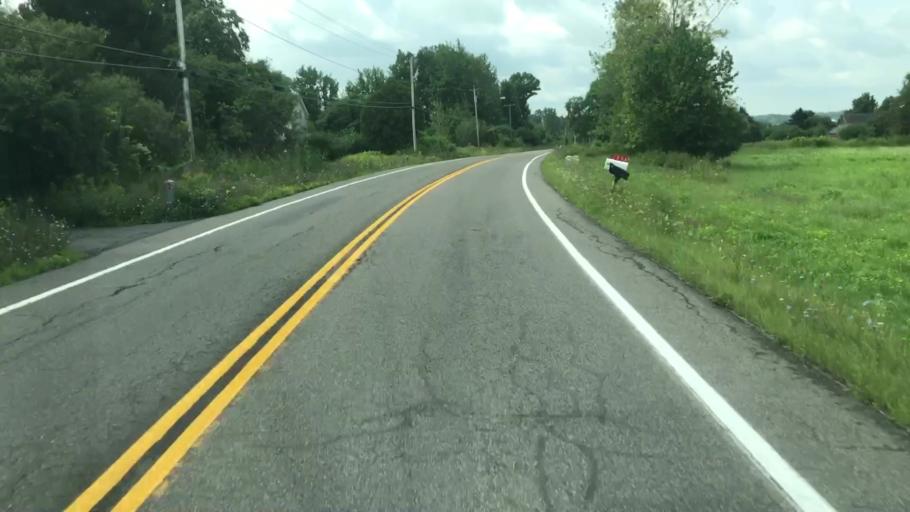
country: US
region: New York
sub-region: Onondaga County
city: Skaneateles
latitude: 42.9696
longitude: -76.4292
